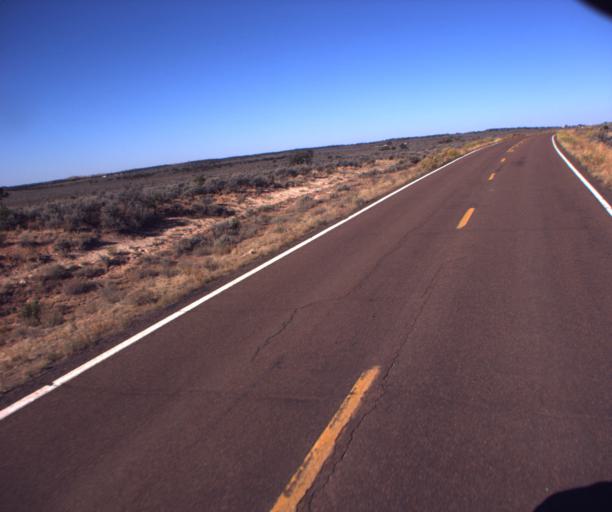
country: US
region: Arizona
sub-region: Apache County
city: Ganado
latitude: 35.7492
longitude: -109.9347
